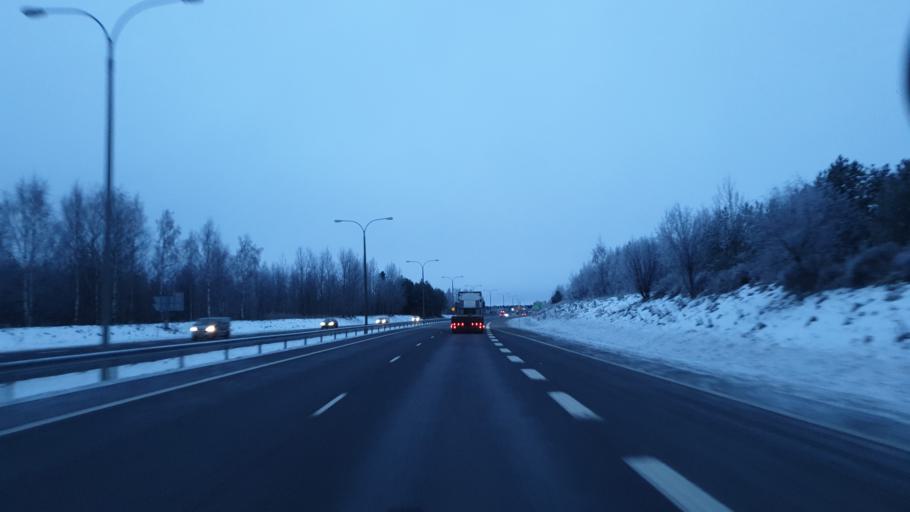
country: FI
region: Northern Ostrobothnia
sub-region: Oulu
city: Kempele
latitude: 64.9017
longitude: 25.5330
